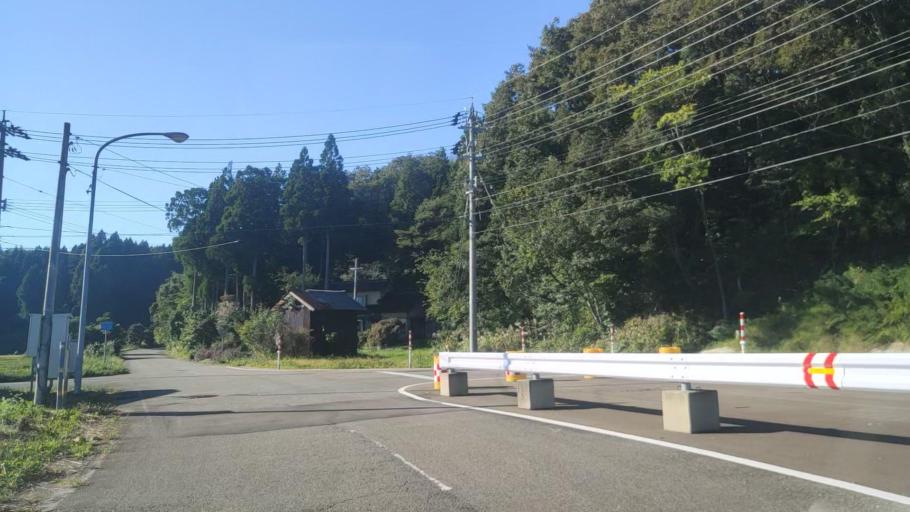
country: JP
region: Ishikawa
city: Nanao
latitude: 37.1160
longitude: 136.8834
